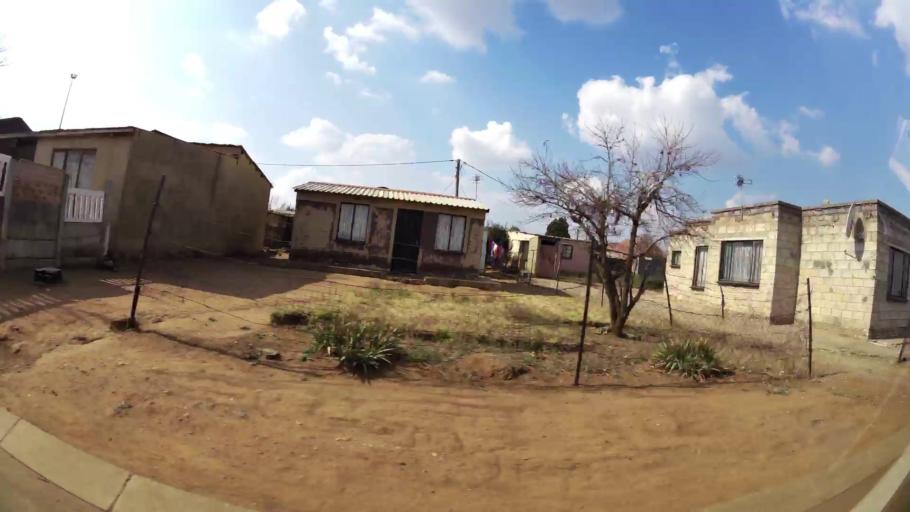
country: ZA
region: Gauteng
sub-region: Ekurhuleni Metropolitan Municipality
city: Springs
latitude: -26.1307
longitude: 28.4726
